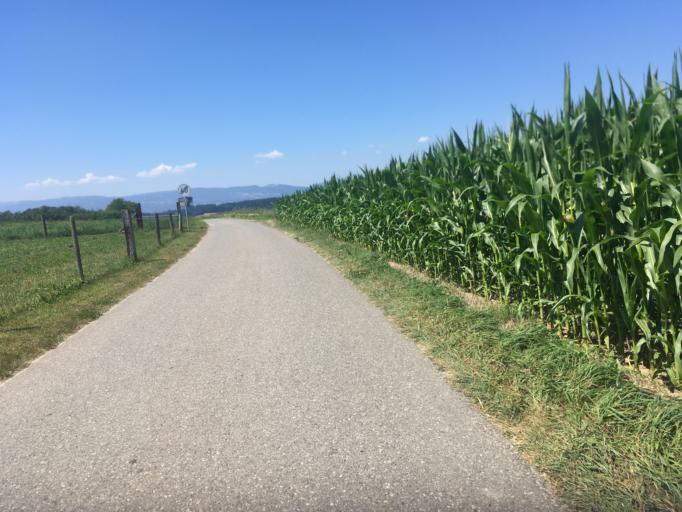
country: CH
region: Solothurn
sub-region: Bezirk Bucheggberg
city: Messen
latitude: 47.0774
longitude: 7.4156
